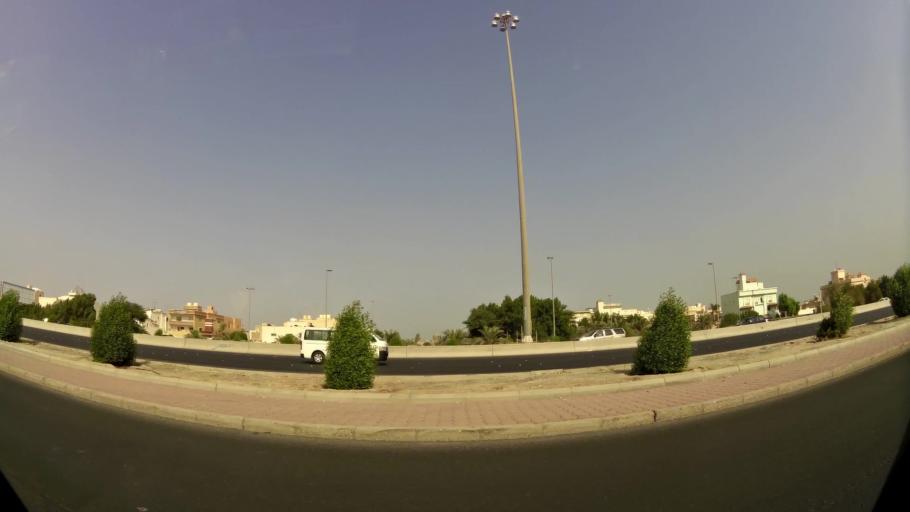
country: KW
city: Bayan
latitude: 29.3090
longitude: 48.0566
